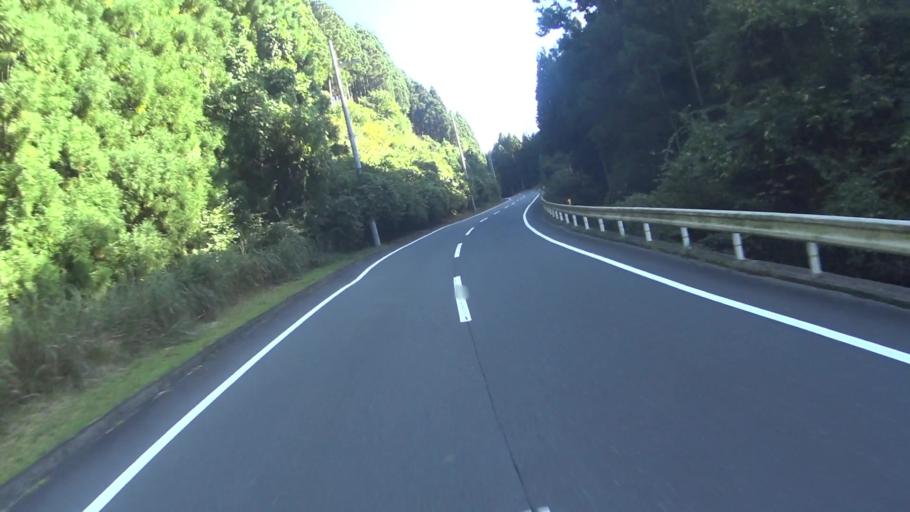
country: JP
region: Kyoto
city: Kameoka
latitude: 35.1207
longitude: 135.5637
